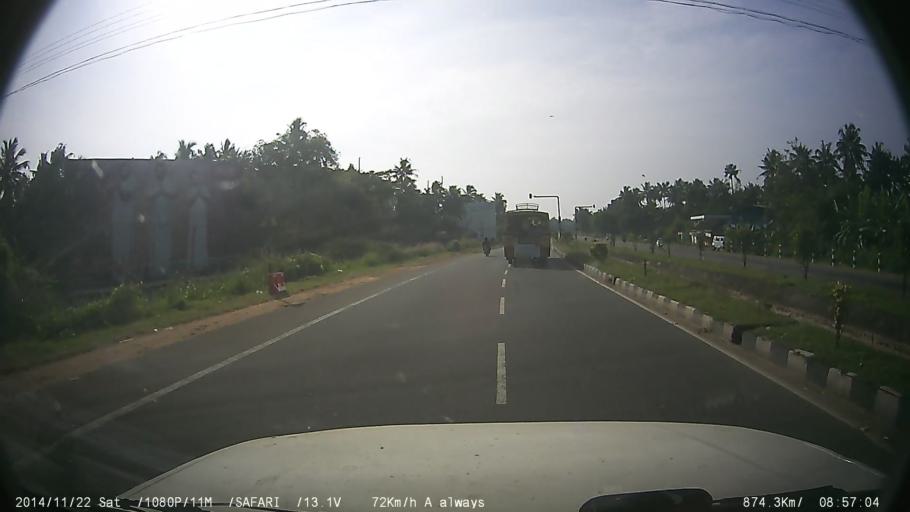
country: IN
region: Kerala
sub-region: Thrissur District
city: Irinjalakuda
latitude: 10.4102
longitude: 76.2736
